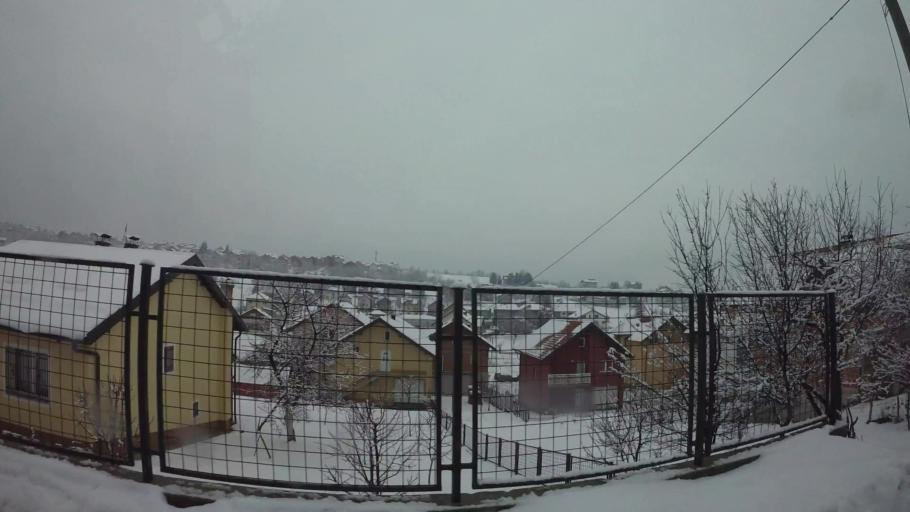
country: BA
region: Federation of Bosnia and Herzegovina
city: Vogosca
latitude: 43.8755
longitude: 18.3203
